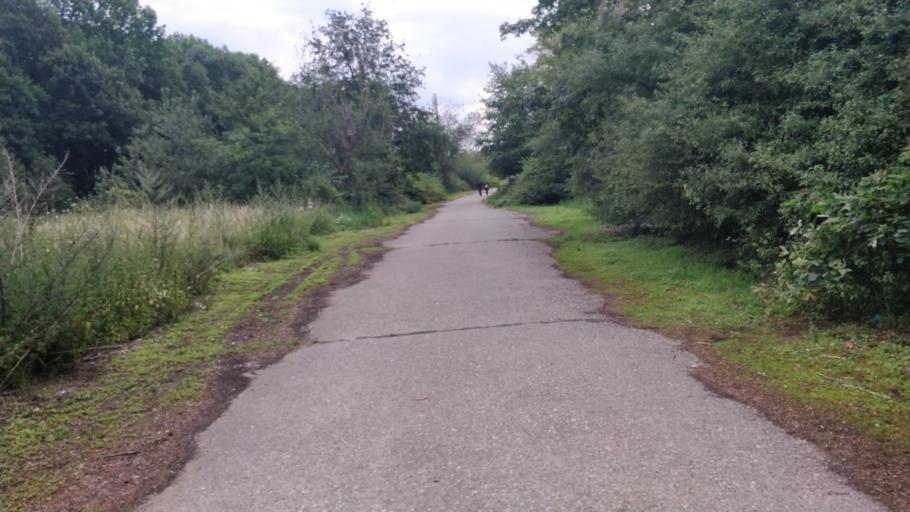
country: DE
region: North Rhine-Westphalia
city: Monheim am Rhein
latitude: 51.0382
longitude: 6.8765
